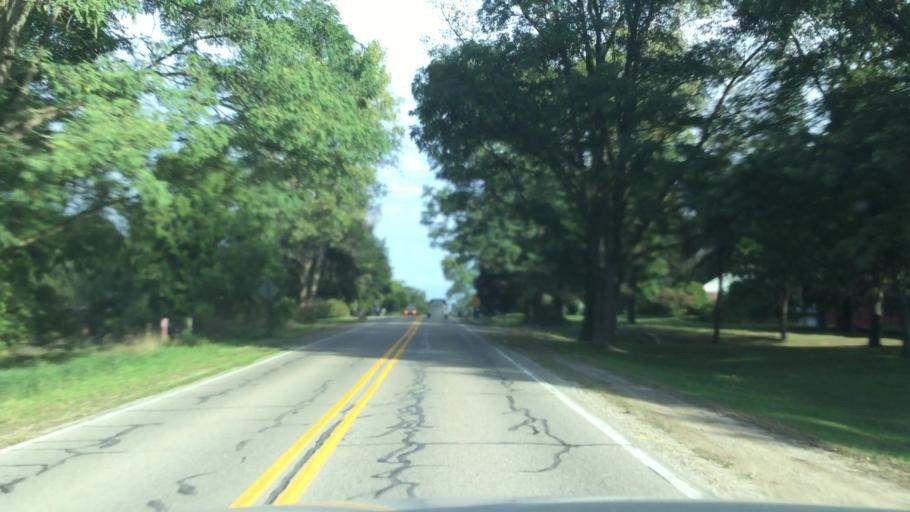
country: US
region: Michigan
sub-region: Livingston County
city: Howell
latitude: 42.5750
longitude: -83.8939
